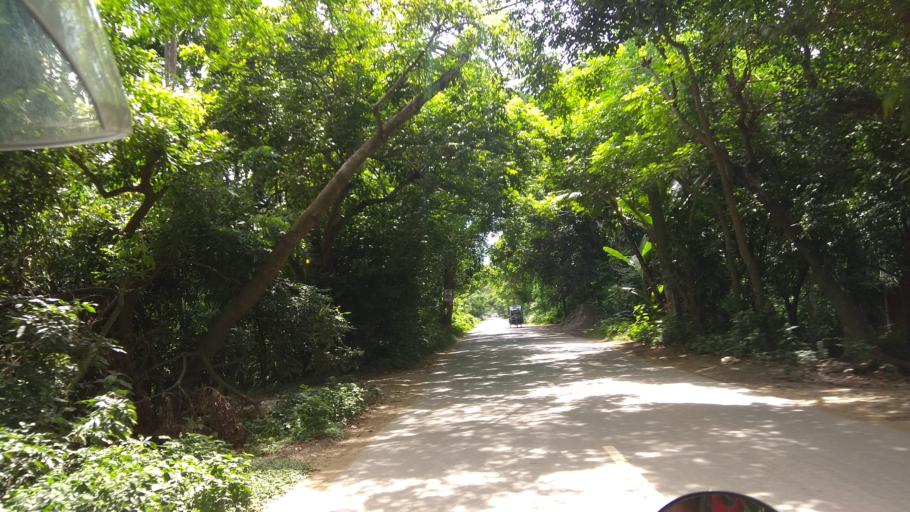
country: BD
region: Khulna
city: Kalia
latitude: 23.1957
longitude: 89.6795
